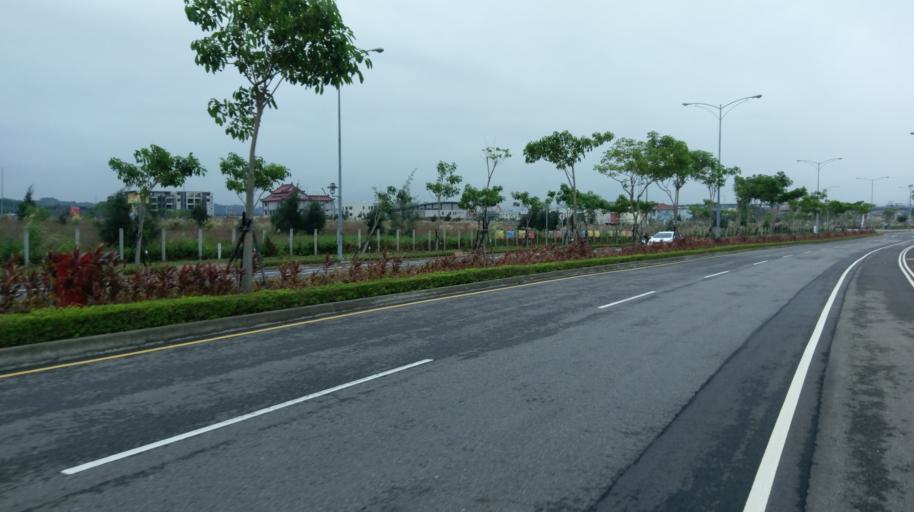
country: TW
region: Taiwan
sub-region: Miaoli
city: Miaoli
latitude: 24.6147
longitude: 120.8251
